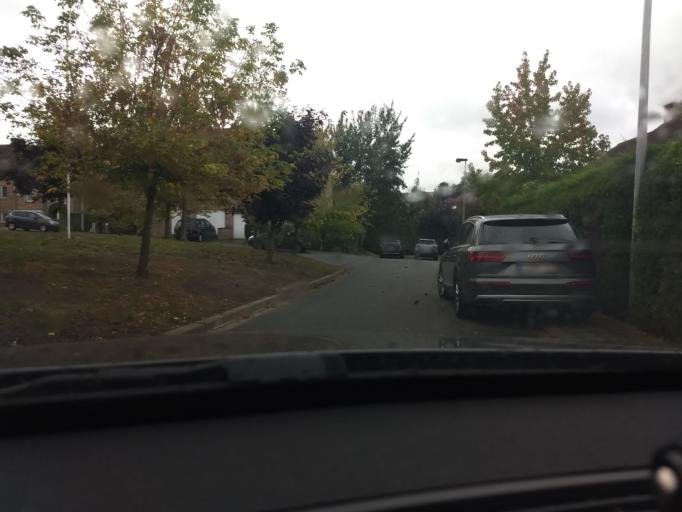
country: BE
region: Wallonia
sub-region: Province du Brabant Wallon
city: Braine-l'Alleud
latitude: 50.6763
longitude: 4.3707
